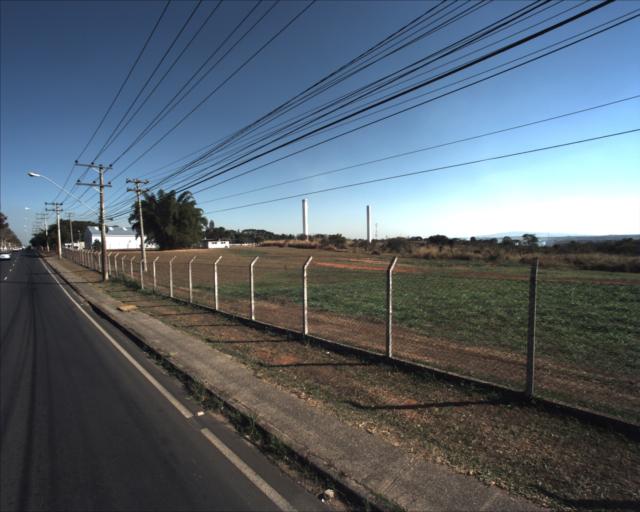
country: BR
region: Sao Paulo
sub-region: Sorocaba
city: Sorocaba
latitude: -23.4327
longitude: -47.4156
